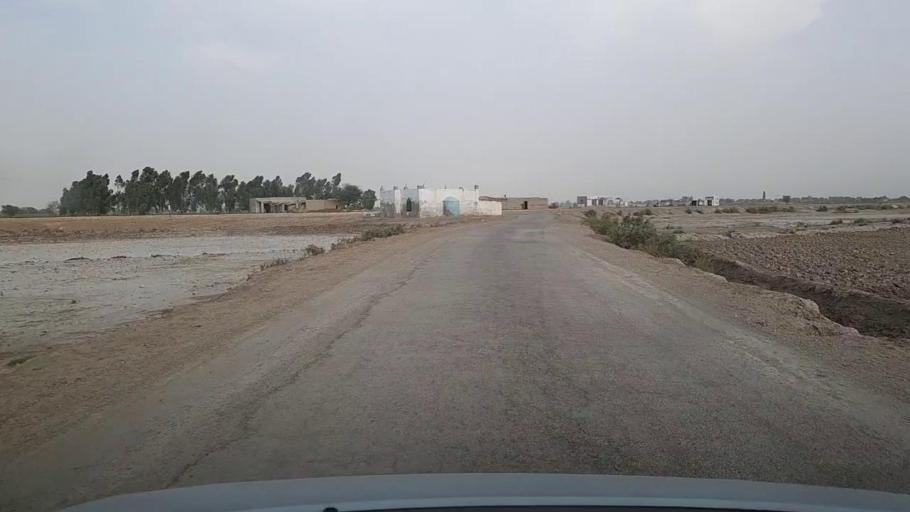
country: PK
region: Sindh
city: Dadu
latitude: 26.8118
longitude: 67.7776
